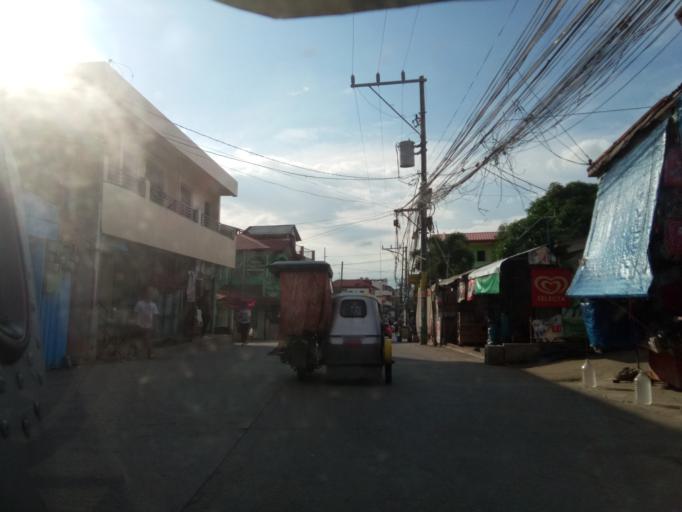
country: PH
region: Calabarzon
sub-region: Province of Cavite
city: Dasmarinas
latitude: 14.2924
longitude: 120.9393
